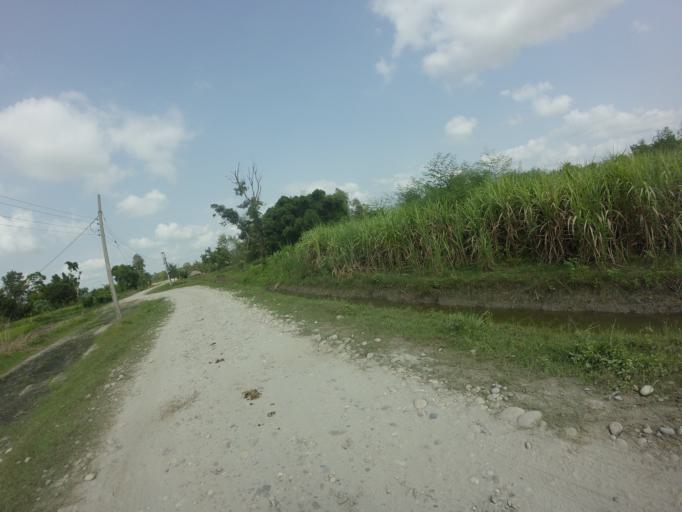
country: NP
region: Far Western
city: Tikapur
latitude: 28.4411
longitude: 81.0704
